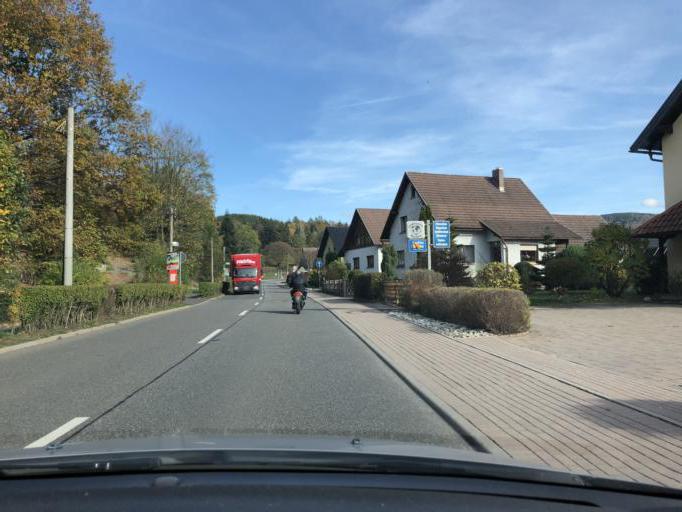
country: DE
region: Thuringia
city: Sankt Kilian
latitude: 50.5040
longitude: 10.8242
